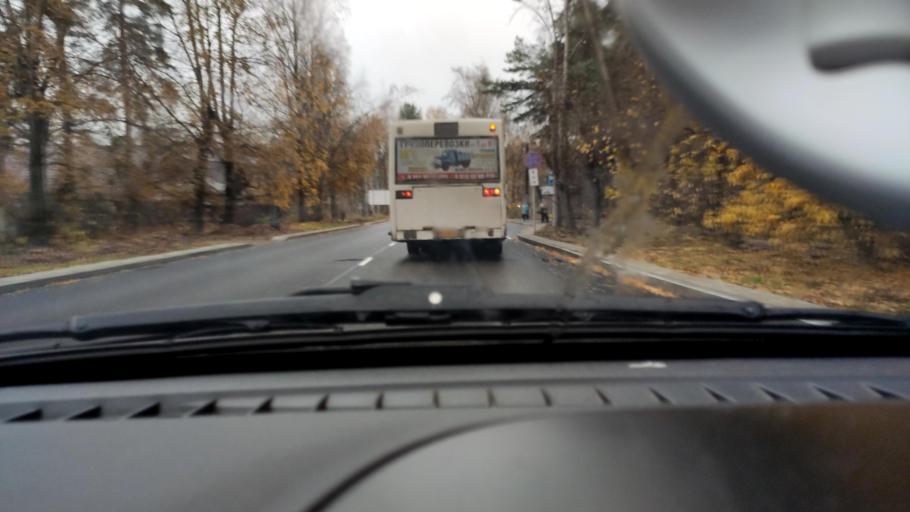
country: RU
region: Perm
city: Kondratovo
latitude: 58.0223
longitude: 56.0127
